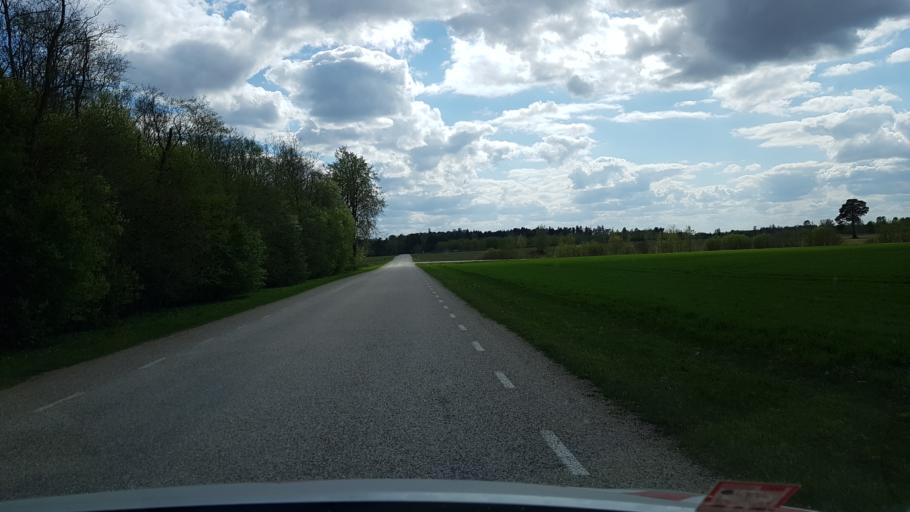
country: EE
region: Tartu
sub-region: Tartu linn
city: Tartu
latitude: 58.3520
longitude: 26.8513
